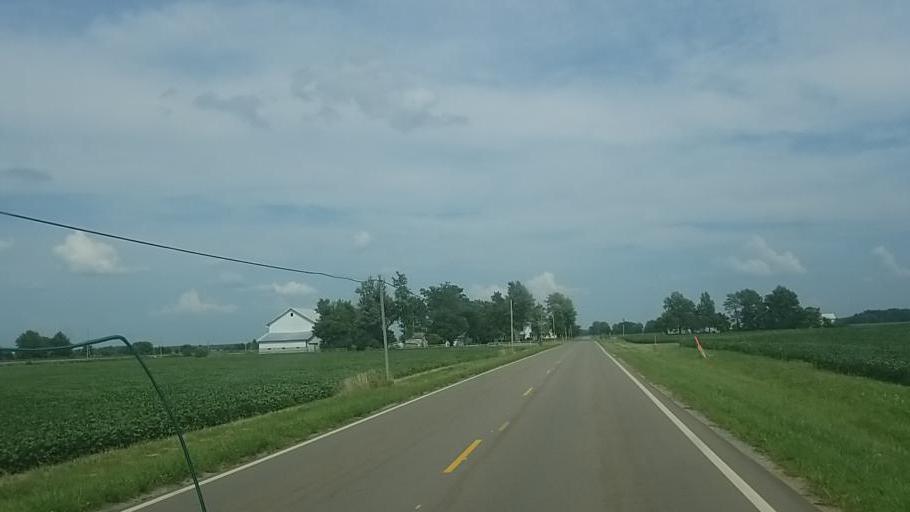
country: US
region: Ohio
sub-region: Hardin County
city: Forest
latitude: 40.8036
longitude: -83.4813
